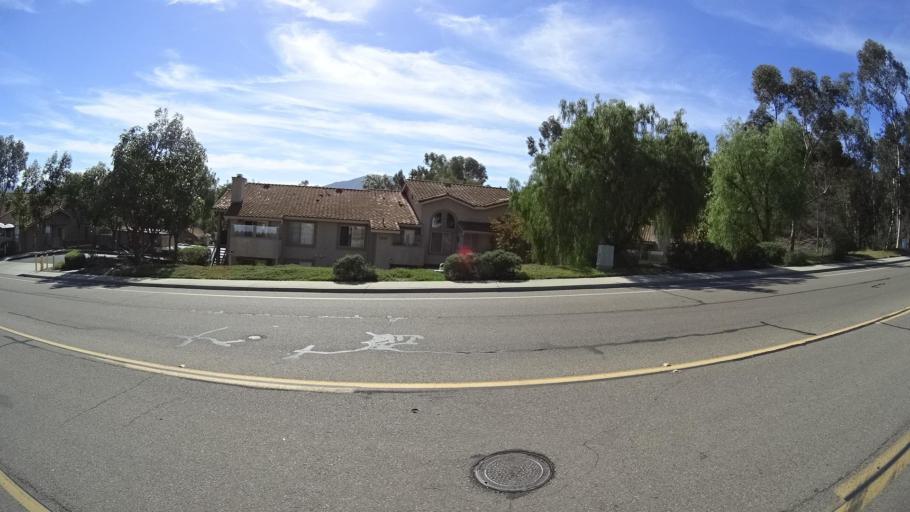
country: US
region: California
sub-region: San Diego County
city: Rancho San Diego
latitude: 32.7513
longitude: -116.9456
